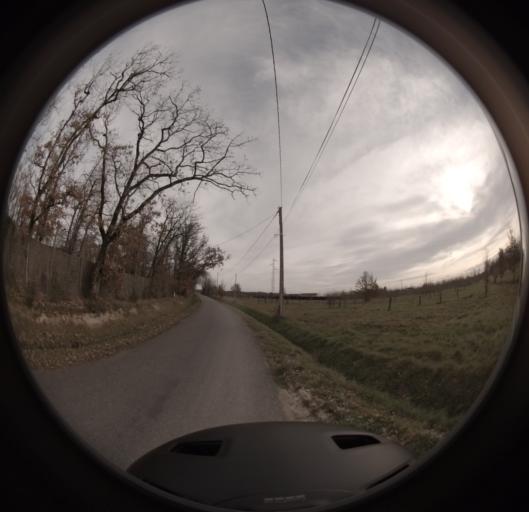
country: FR
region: Midi-Pyrenees
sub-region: Departement du Tarn-et-Garonne
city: Montbeton
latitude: 43.9934
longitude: 1.2846
